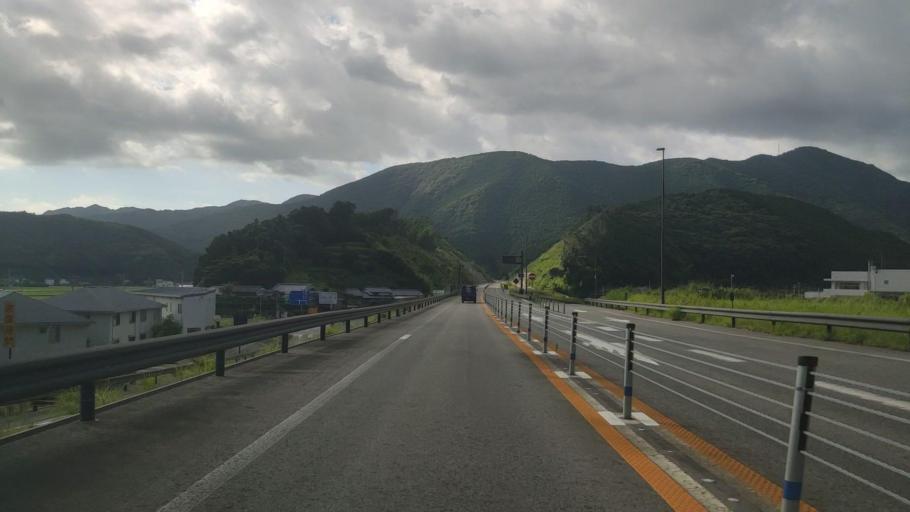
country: JP
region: Wakayama
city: Tanabe
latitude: 33.5548
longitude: 135.5103
